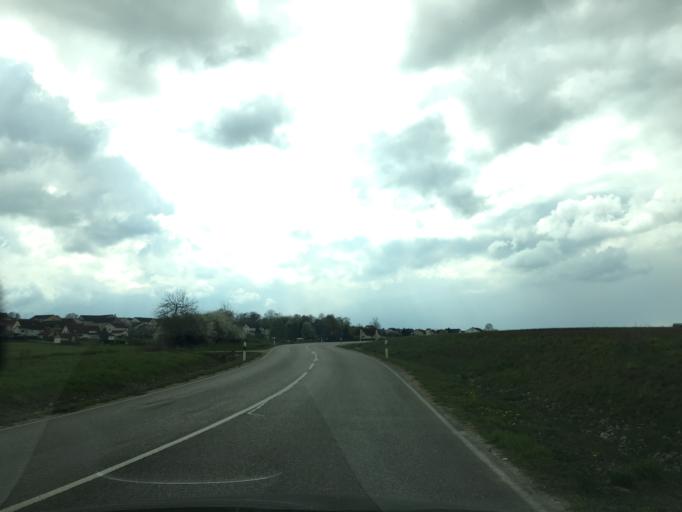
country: DE
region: Bavaria
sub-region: Regierungsbezirk Mittelfranken
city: Langenaltheim
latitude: 48.8980
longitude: 10.9349
